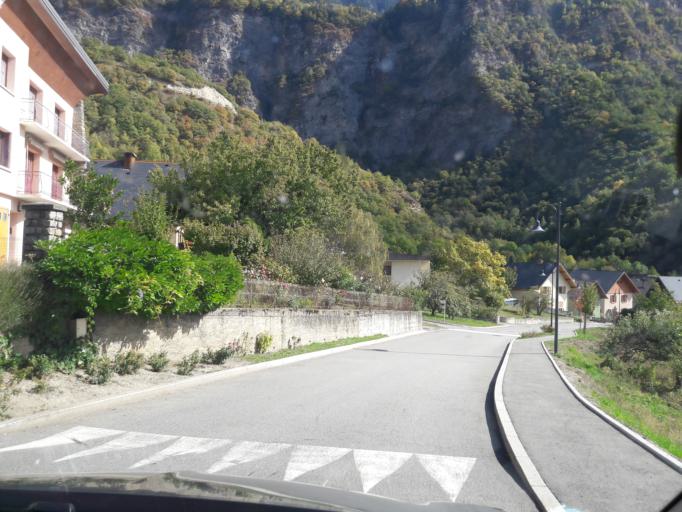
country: FR
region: Rhone-Alpes
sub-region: Departement de la Savoie
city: Saint-Jean-de-Maurienne
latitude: 45.3008
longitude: 6.3636
